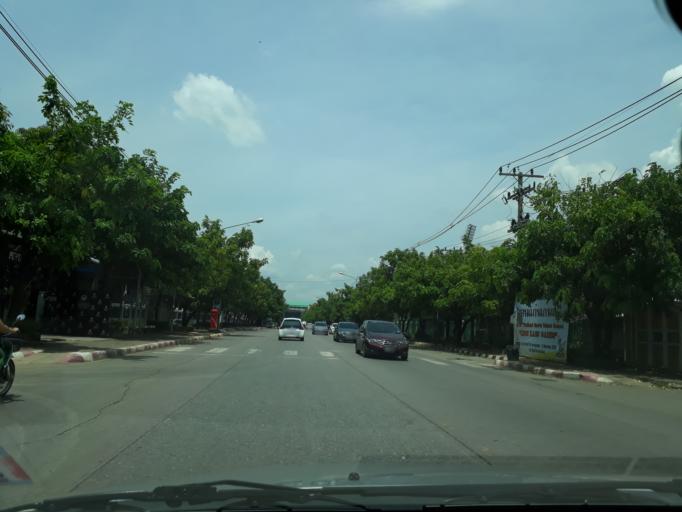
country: TH
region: Khon Kaen
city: Khon Kaen
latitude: 16.4144
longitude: 102.8269
